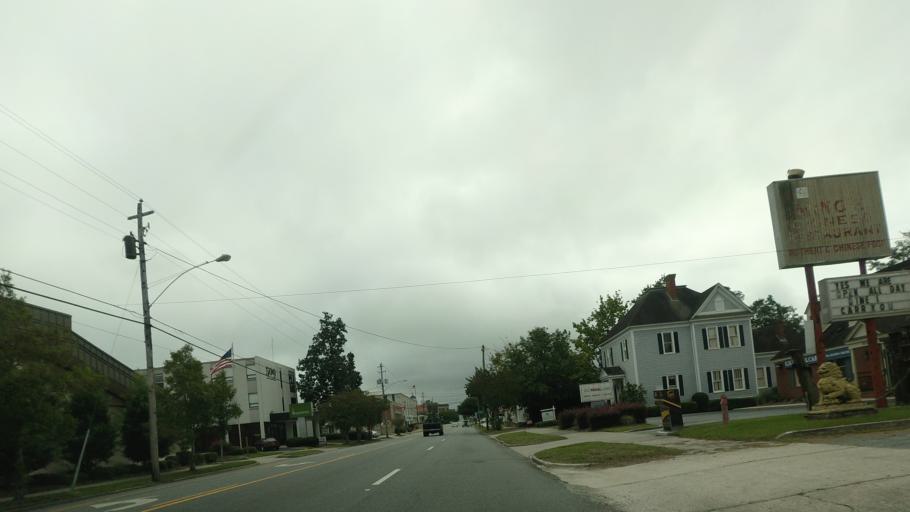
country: US
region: Georgia
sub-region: Lowndes County
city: Valdosta
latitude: 30.8362
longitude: -83.2817
